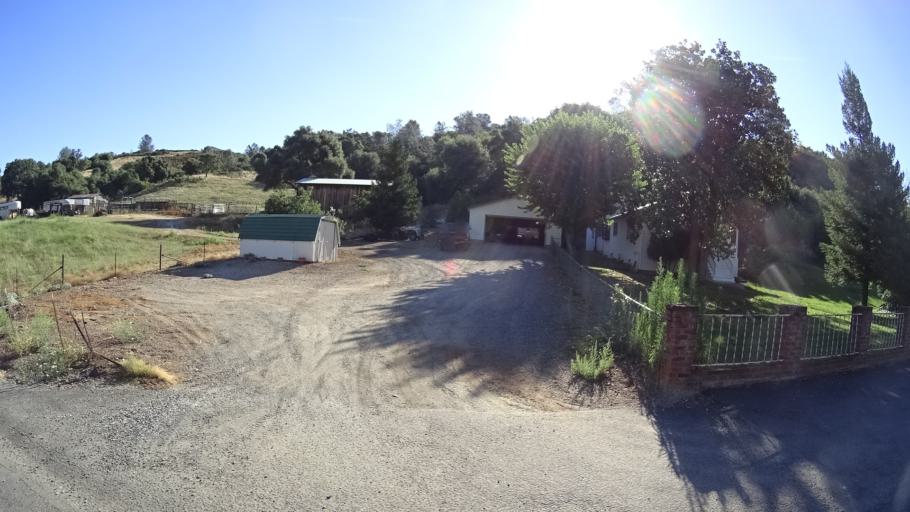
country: US
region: California
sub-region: Calaveras County
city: Angels Camp
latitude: 38.0394
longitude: -120.5053
